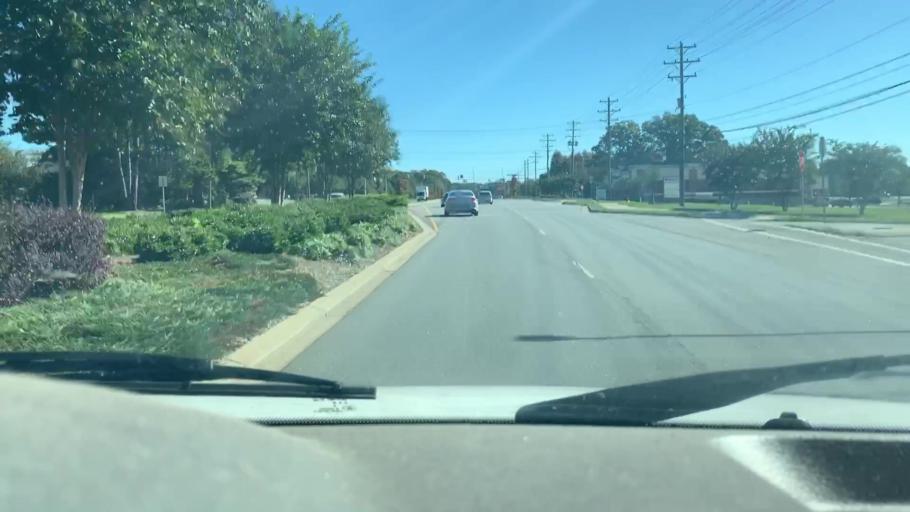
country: US
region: North Carolina
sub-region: Mecklenburg County
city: Huntersville
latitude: 35.4410
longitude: -80.8470
